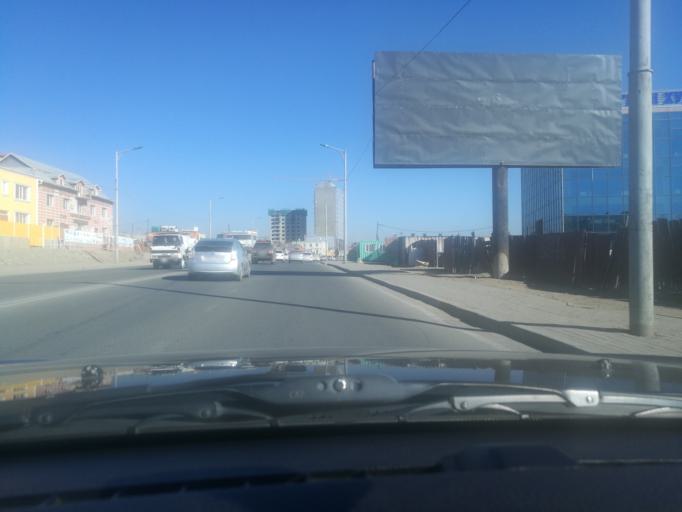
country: MN
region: Ulaanbaatar
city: Ulaanbaatar
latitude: 47.9311
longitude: 106.9051
